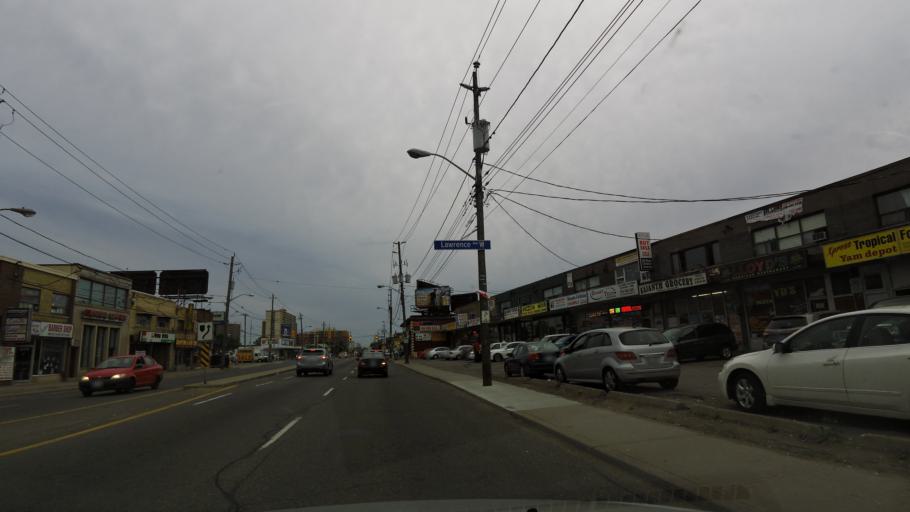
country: CA
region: Ontario
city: Etobicoke
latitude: 43.7039
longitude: -79.5041
